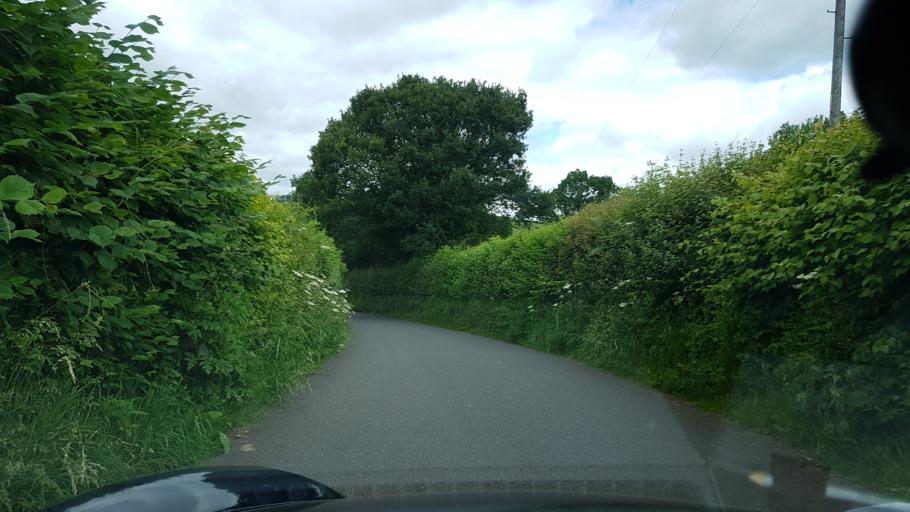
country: GB
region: Wales
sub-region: Monmouthshire
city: Llanarth
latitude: 51.8536
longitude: -2.9012
